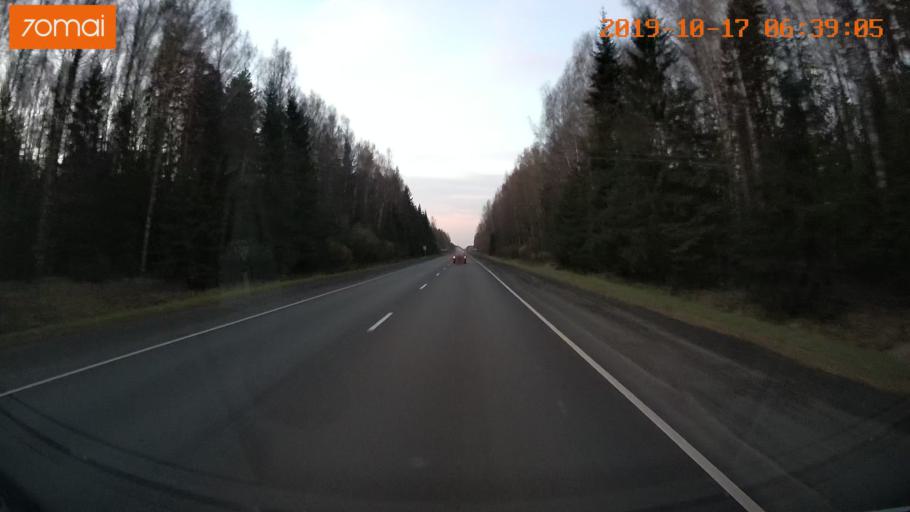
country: RU
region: Ivanovo
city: Novoye Leushino
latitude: 56.6476
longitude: 40.5818
